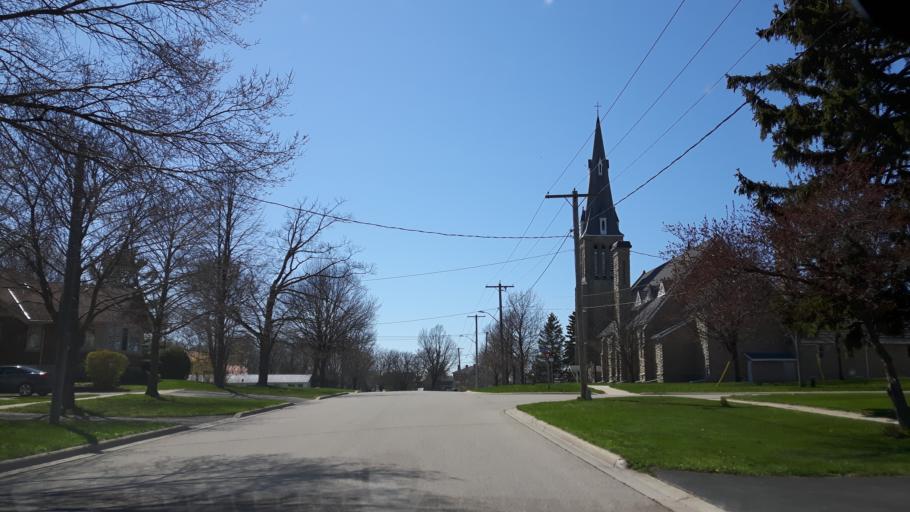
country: CA
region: Ontario
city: Goderich
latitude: 43.7480
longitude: -81.7095
